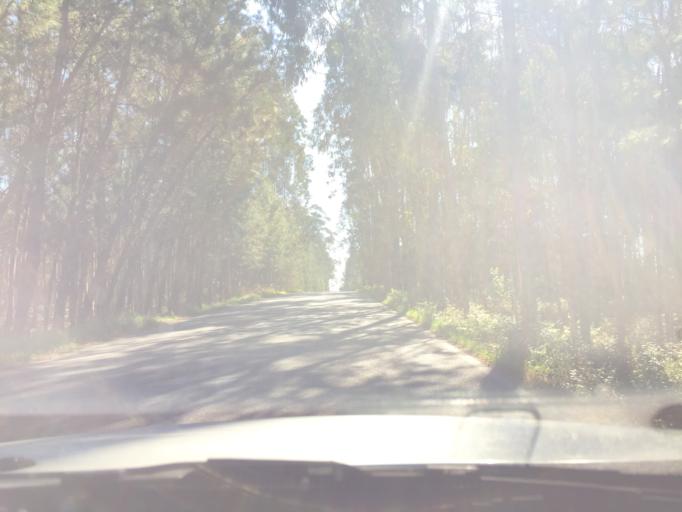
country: PT
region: Coimbra
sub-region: Cantanhede
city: Cantanhede
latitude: 40.4231
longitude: -8.5825
